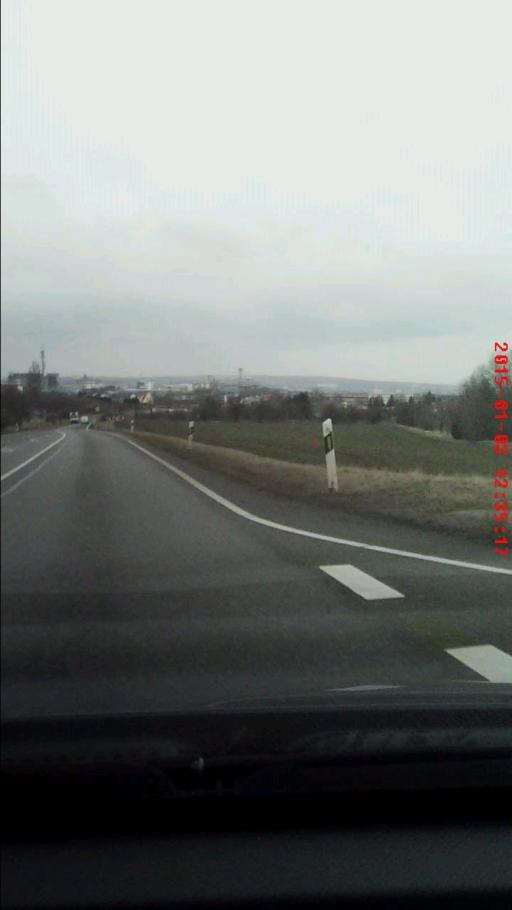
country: DE
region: Thuringia
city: Monchenholzhausen
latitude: 50.9451
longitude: 11.1123
